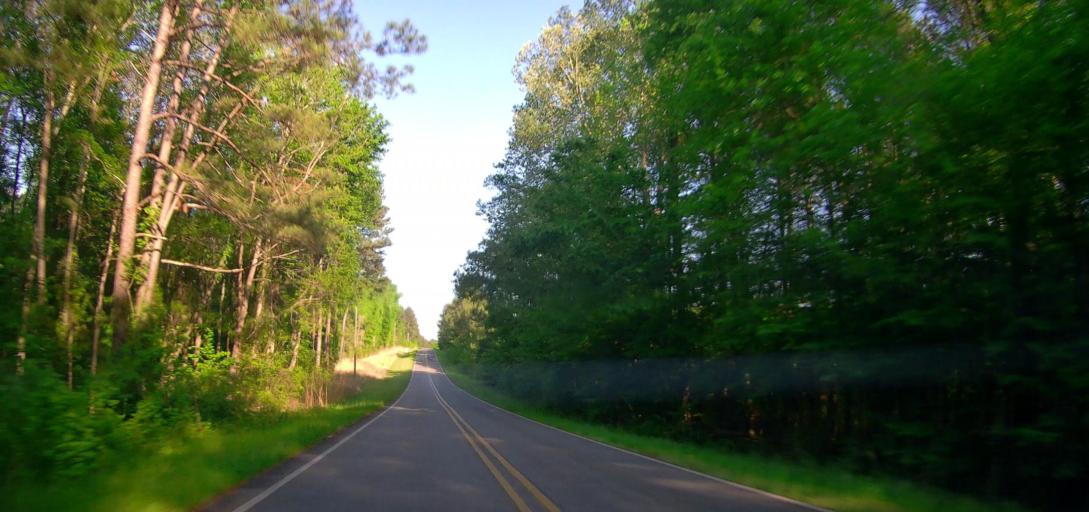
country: US
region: Georgia
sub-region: Putnam County
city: Eatonton
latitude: 33.2846
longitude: -83.3228
